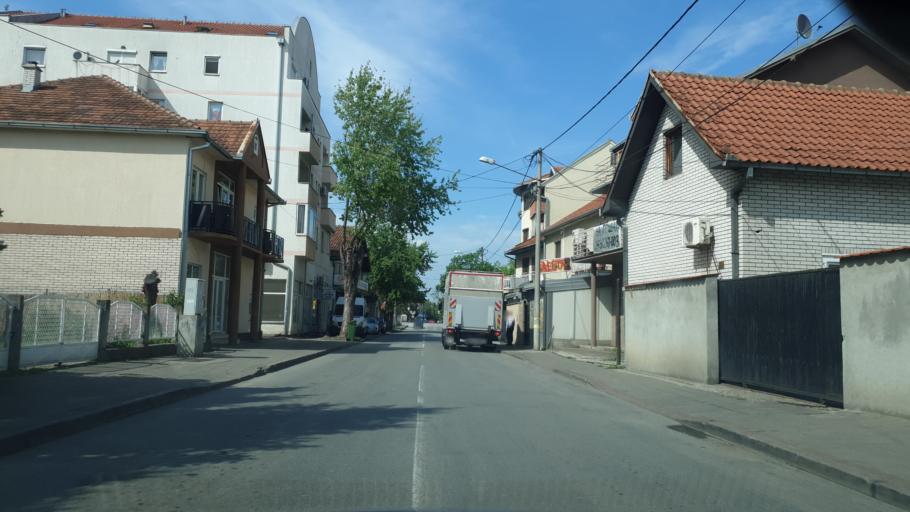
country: RS
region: Central Serbia
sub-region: Belgrade
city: Obrenovac
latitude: 44.6532
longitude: 20.1931
